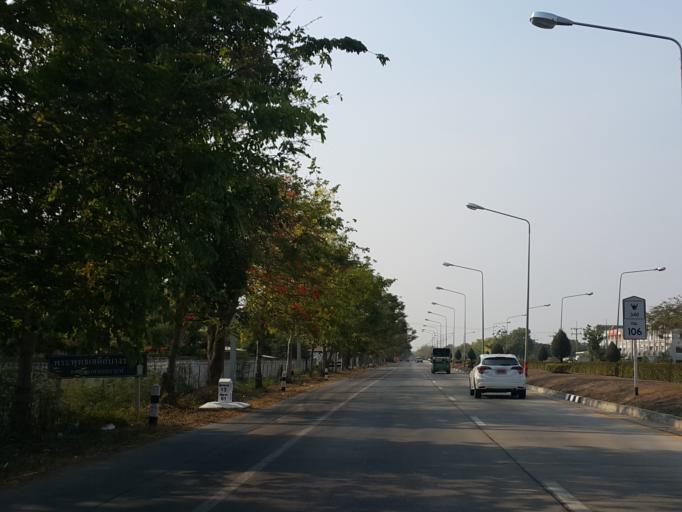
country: TH
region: Suphan Buri
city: Sam Chuk
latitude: 14.7673
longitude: 100.0926
